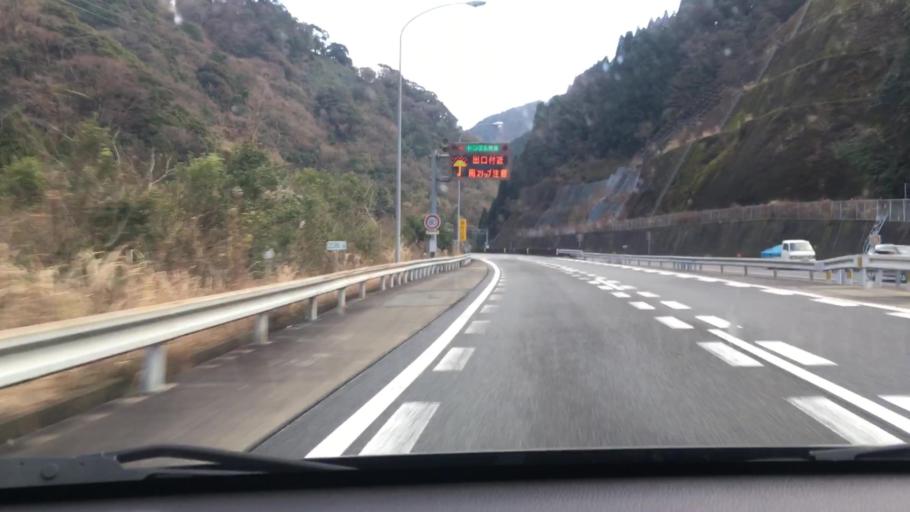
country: JP
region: Kumamoto
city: Hitoyoshi
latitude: 32.3391
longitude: 130.7312
